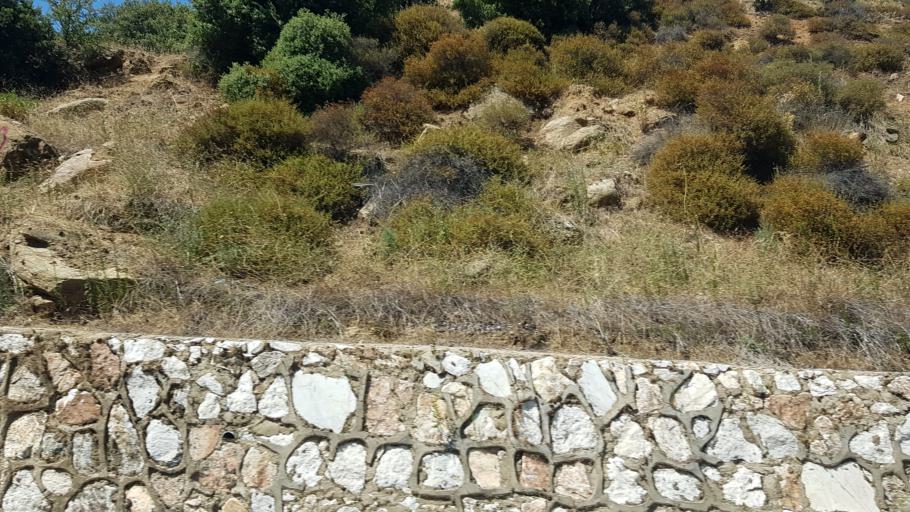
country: TR
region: Aydin
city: Akcaova
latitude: 37.5059
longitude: 28.1026
